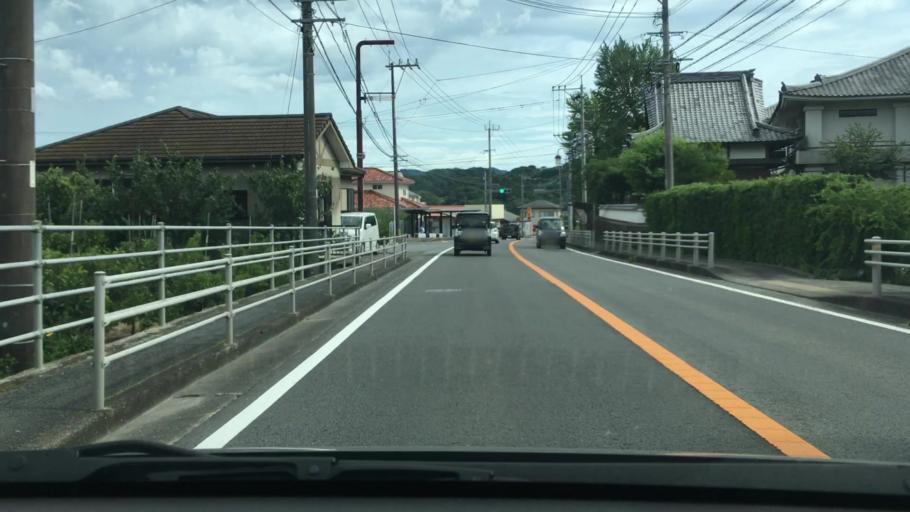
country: JP
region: Nagasaki
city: Togitsu
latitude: 32.9003
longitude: 129.7807
